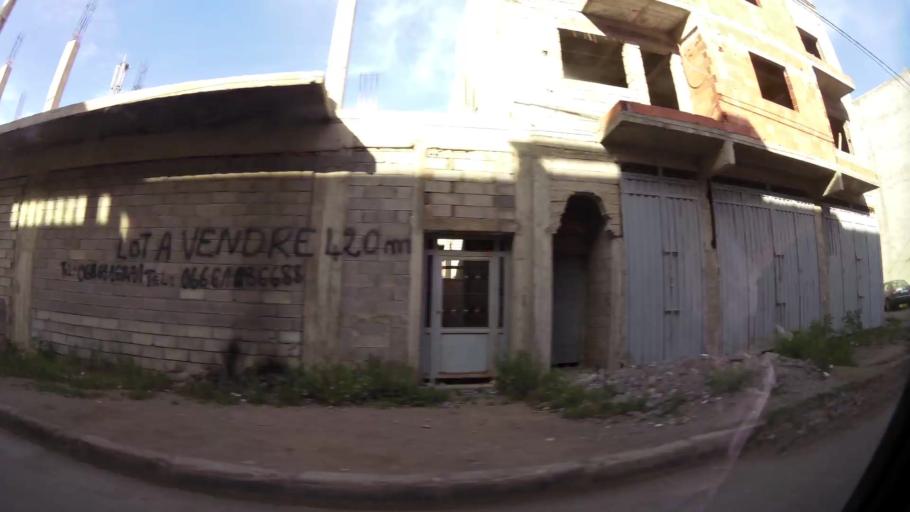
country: MA
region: Marrakech-Tensift-Al Haouz
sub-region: Marrakech
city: Marrakesh
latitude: 31.6794
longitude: -8.0423
